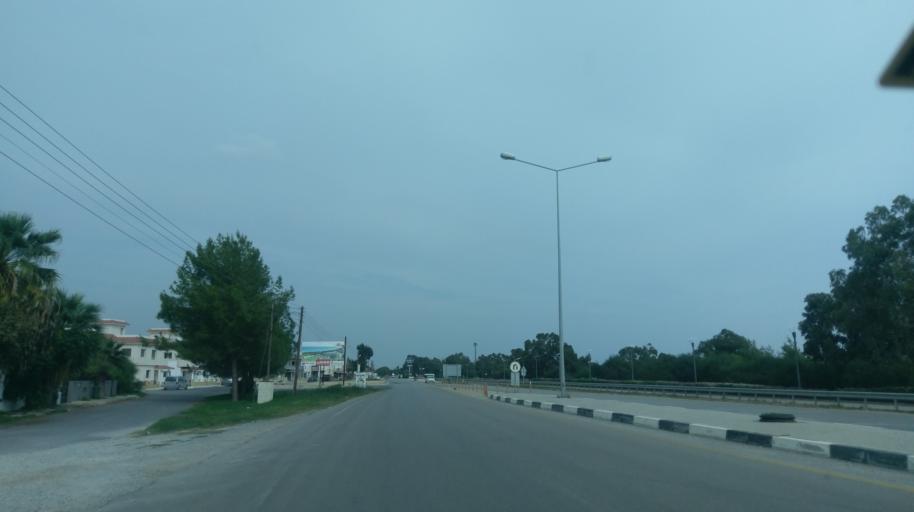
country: CY
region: Ammochostos
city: Trikomo
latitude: 35.2792
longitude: 33.9206
